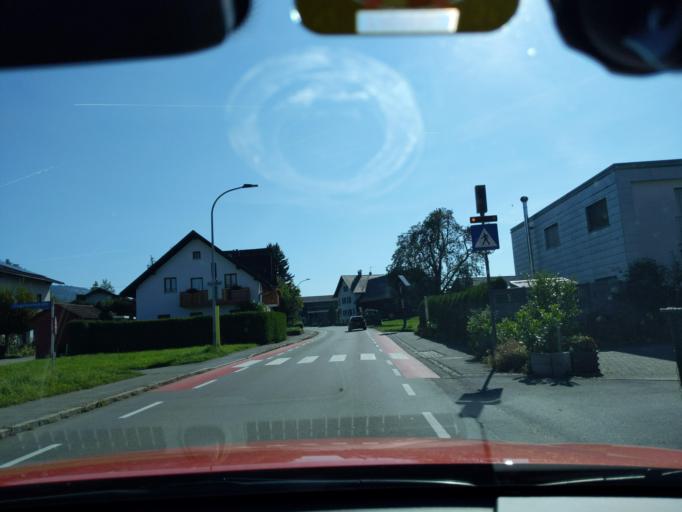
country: AT
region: Vorarlberg
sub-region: Politischer Bezirk Bregenz
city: Horbranz
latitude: 47.5518
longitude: 9.7512
